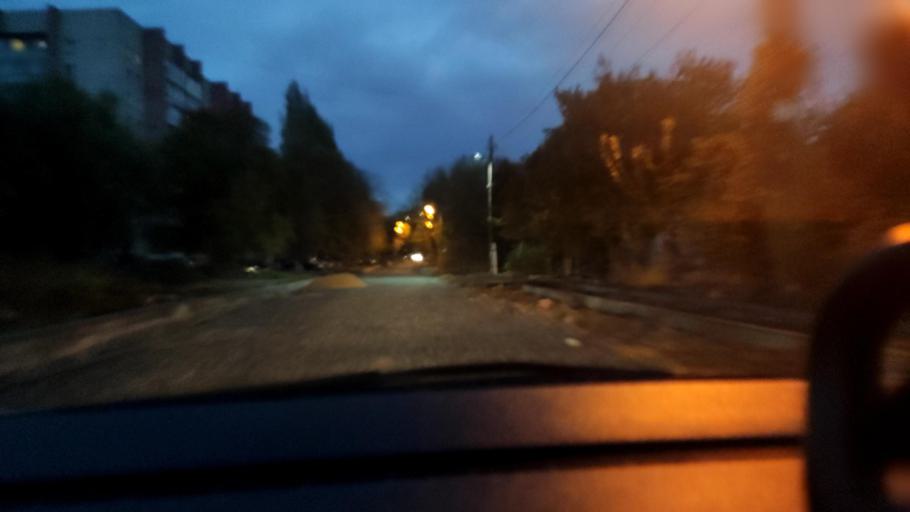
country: RU
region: Voronezj
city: Voronezh
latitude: 51.6906
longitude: 39.1974
